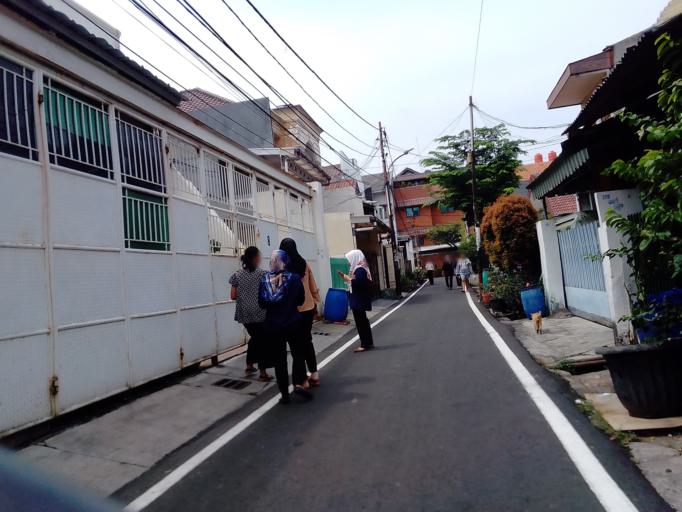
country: ID
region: Jakarta Raya
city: Jakarta
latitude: -6.1731
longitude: 106.8101
